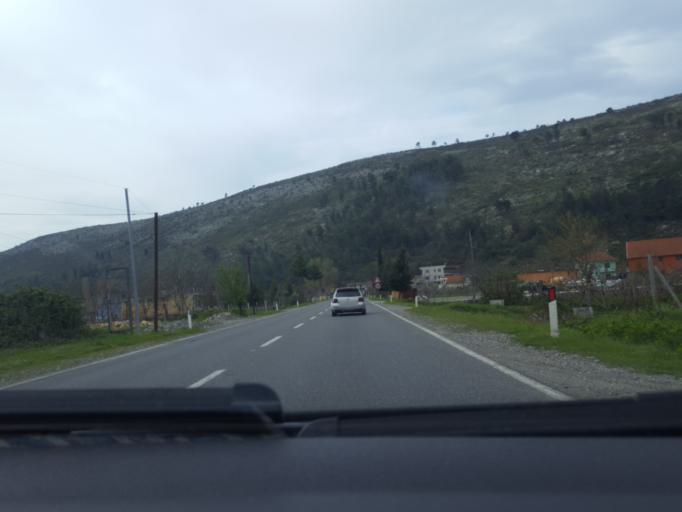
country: AL
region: Lezhe
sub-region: Rrethi i Lezhes
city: Balldreni i Ri
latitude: 41.8053
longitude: 19.6320
